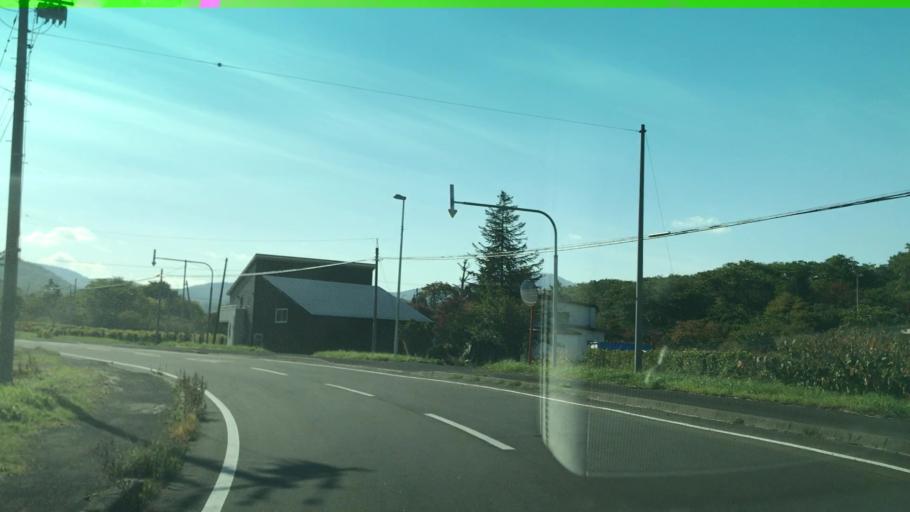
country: JP
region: Hokkaido
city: Yoichi
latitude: 43.1690
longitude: 140.8206
